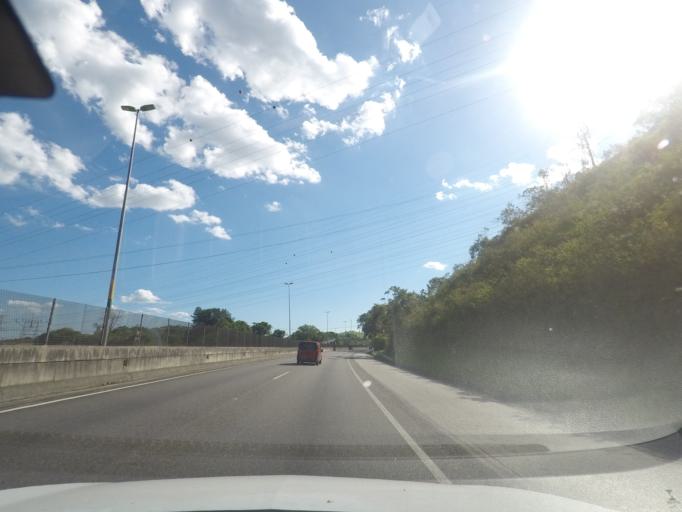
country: BR
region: Rio de Janeiro
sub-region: Guapimirim
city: Guapimirim
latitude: -22.6042
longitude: -43.0260
